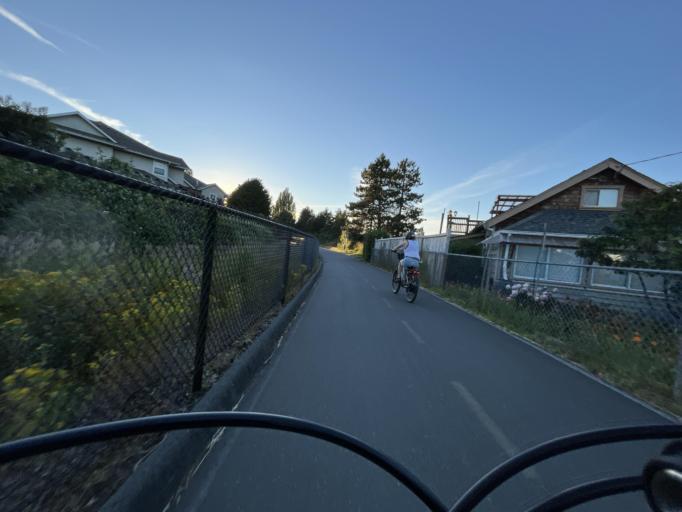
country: CA
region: British Columbia
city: Victoria
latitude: 48.4328
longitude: -123.3903
